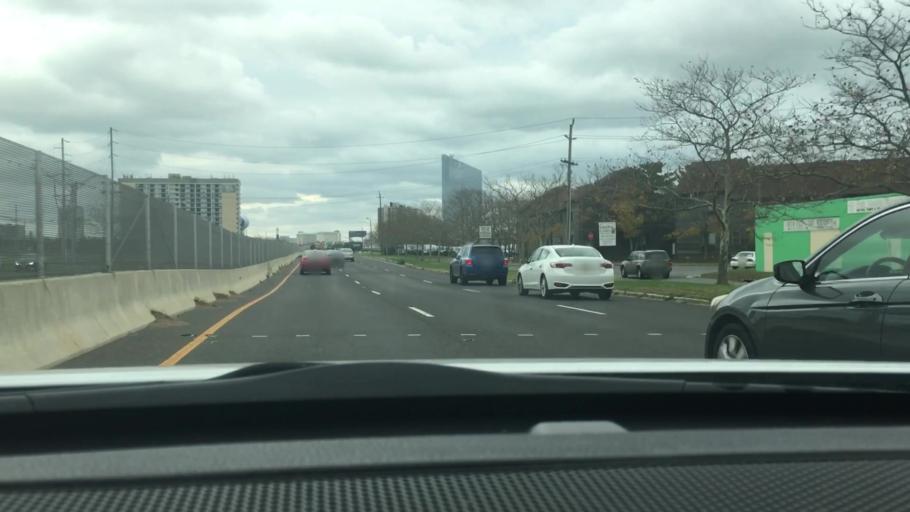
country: US
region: New Jersey
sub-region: Atlantic County
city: Atlantic City
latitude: 39.3723
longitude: -74.4359
